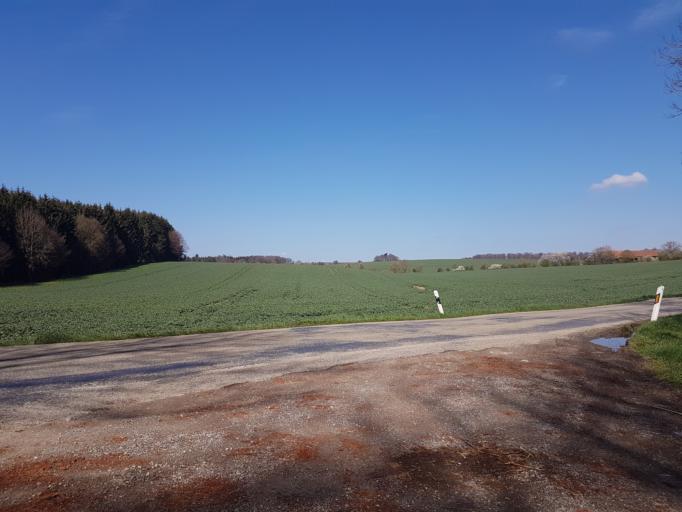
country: DE
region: Baden-Wuerttemberg
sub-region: Regierungsbezirk Stuttgart
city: Jagsthausen
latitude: 49.3423
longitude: 9.4841
